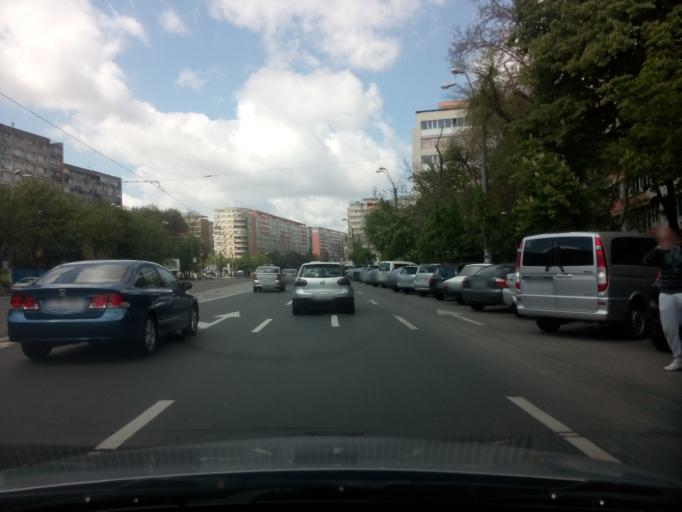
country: RO
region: Bucuresti
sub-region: Municipiul Bucuresti
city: Bucharest
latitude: 44.4423
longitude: 26.1305
